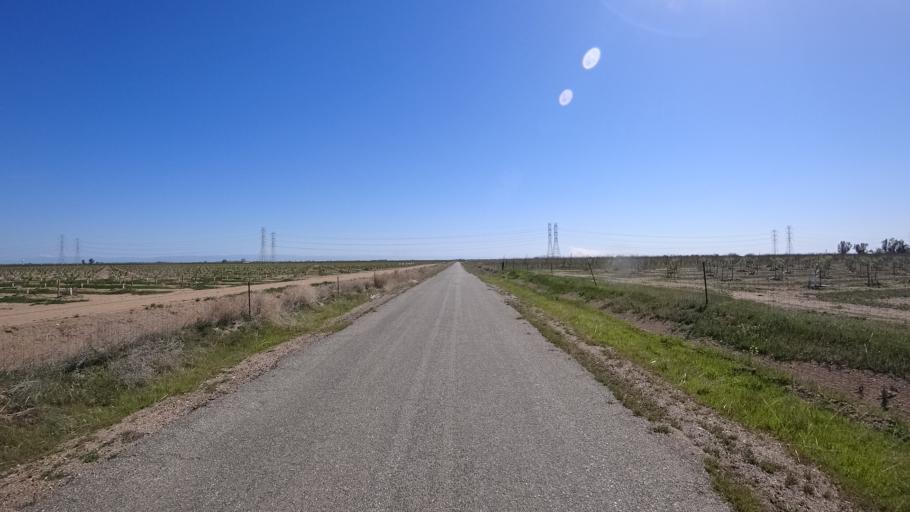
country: US
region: California
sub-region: Glenn County
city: Orland
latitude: 39.6539
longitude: -122.2684
